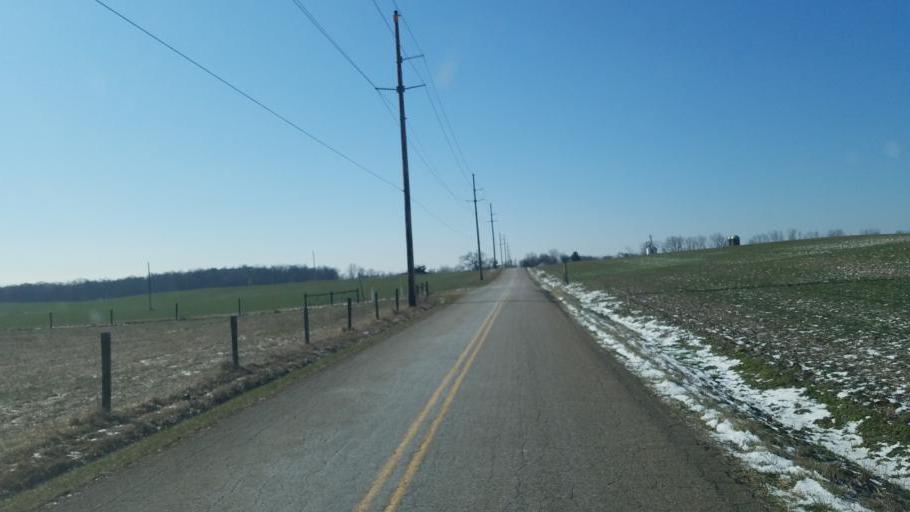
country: US
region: Ohio
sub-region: Licking County
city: Utica
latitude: 40.3013
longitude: -82.4735
